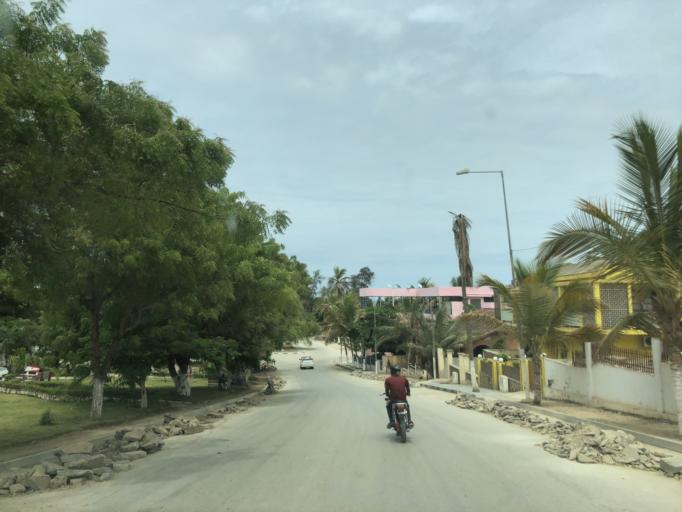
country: AO
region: Cuanza Sul
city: Sumbe
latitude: -11.1957
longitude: 13.8371
